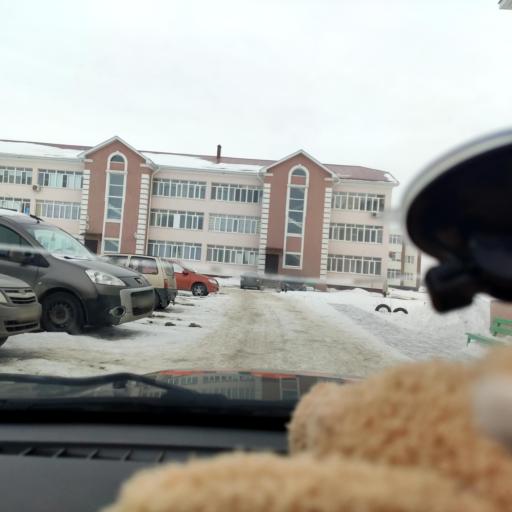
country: RU
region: Samara
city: Podstepki
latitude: 53.5292
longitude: 49.1820
